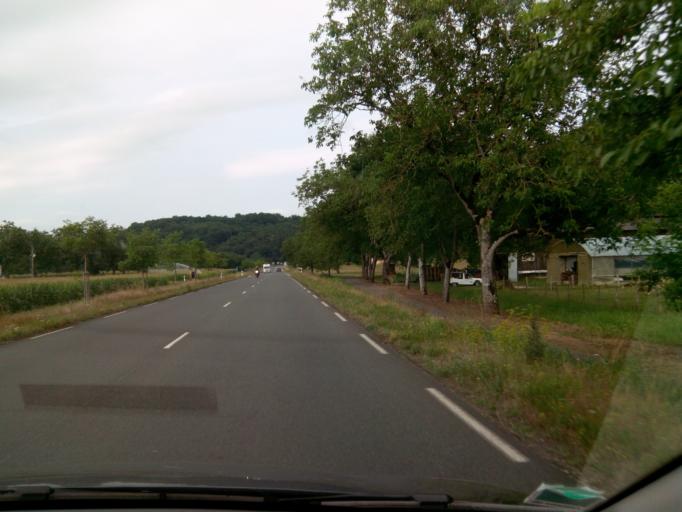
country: FR
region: Aquitaine
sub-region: Departement de la Dordogne
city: Carsac-Aillac
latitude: 44.8497
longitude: 1.3194
